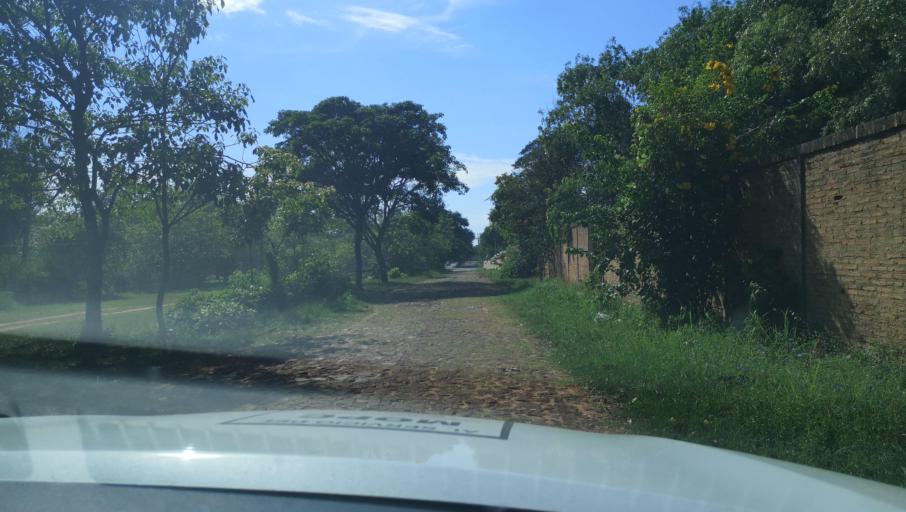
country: PY
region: Misiones
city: Santa Maria
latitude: -26.8926
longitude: -57.0334
